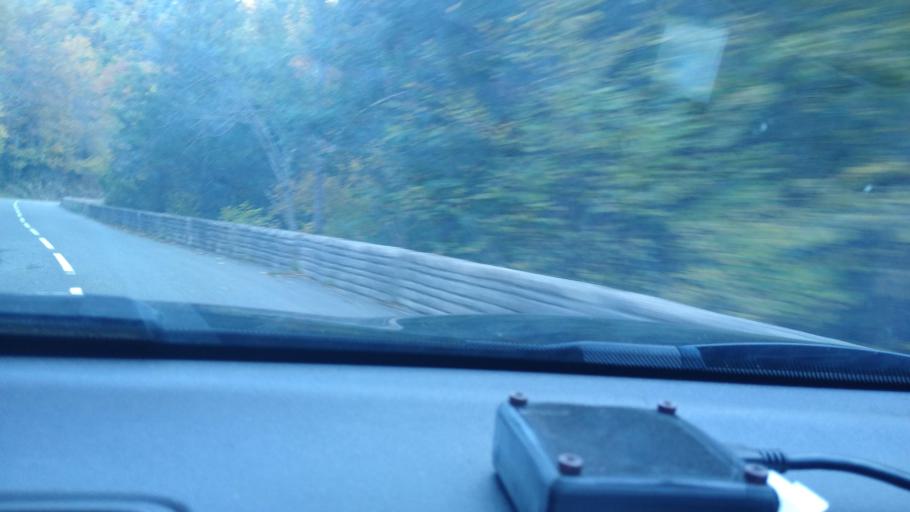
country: FR
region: Languedoc-Roussillon
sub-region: Departement de l'Aude
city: Quillan
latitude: 42.7264
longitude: 2.1124
